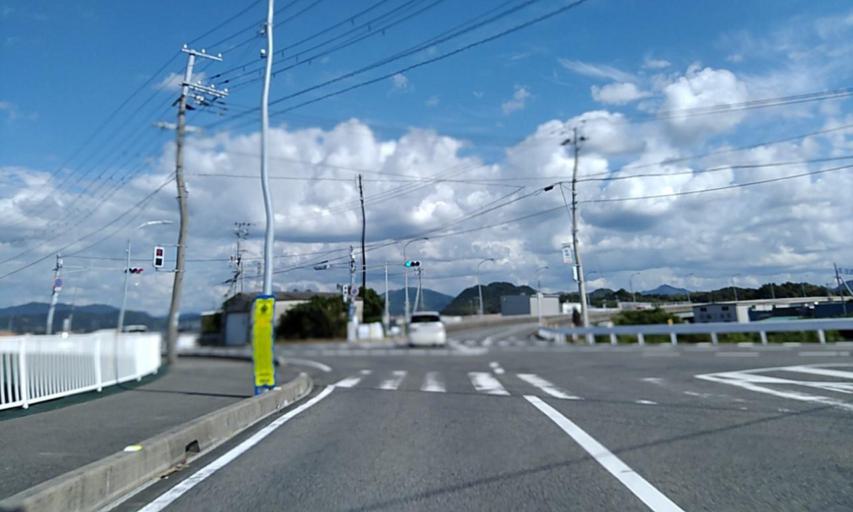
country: JP
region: Wakayama
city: Gobo
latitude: 33.8919
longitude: 135.1643
